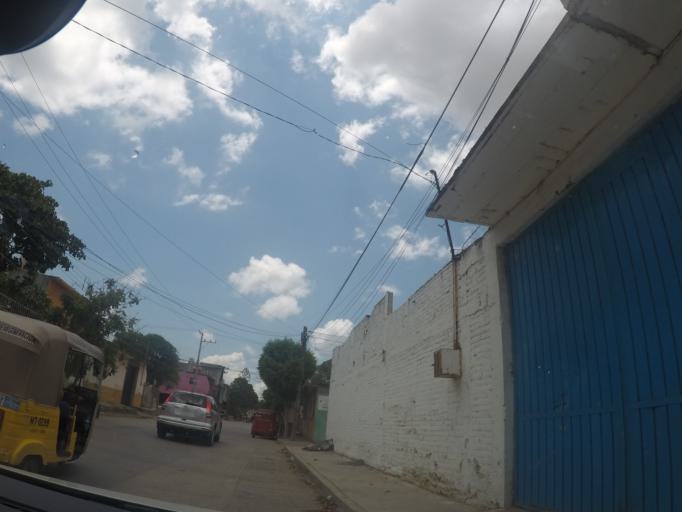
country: MX
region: Oaxaca
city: Juchitan de Zaragoza
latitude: 16.4293
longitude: -95.0219
